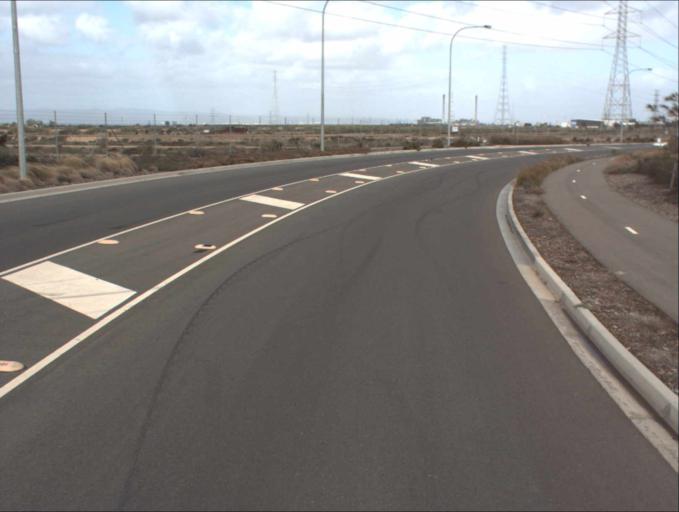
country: AU
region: South Australia
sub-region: Port Adelaide Enfield
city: Birkenhead
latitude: -34.7697
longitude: 138.5100
